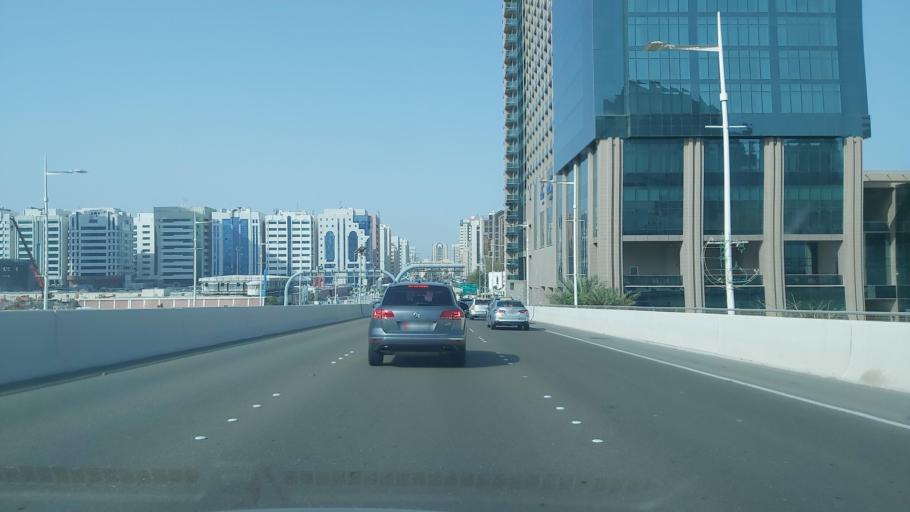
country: AE
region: Abu Dhabi
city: Abu Dhabi
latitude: 24.4944
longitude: 54.3862
